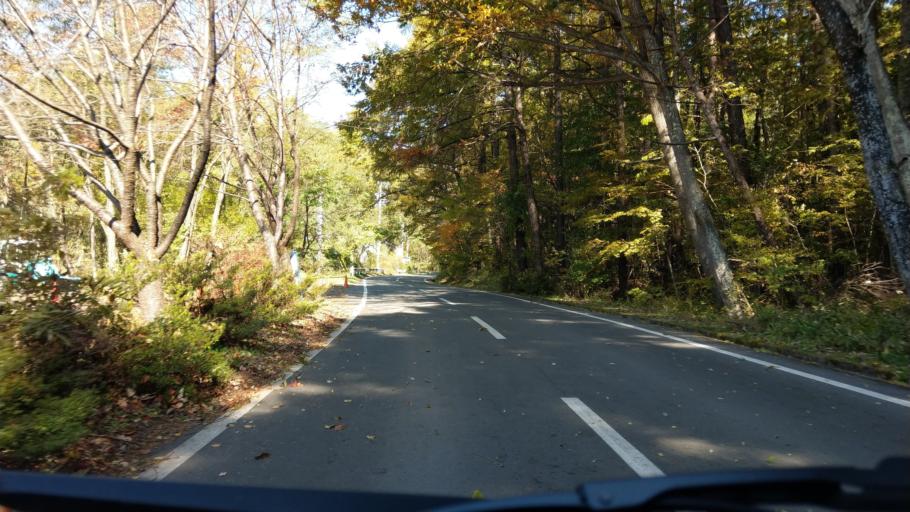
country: JP
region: Nagano
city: Komoro
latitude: 36.3602
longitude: 138.4543
